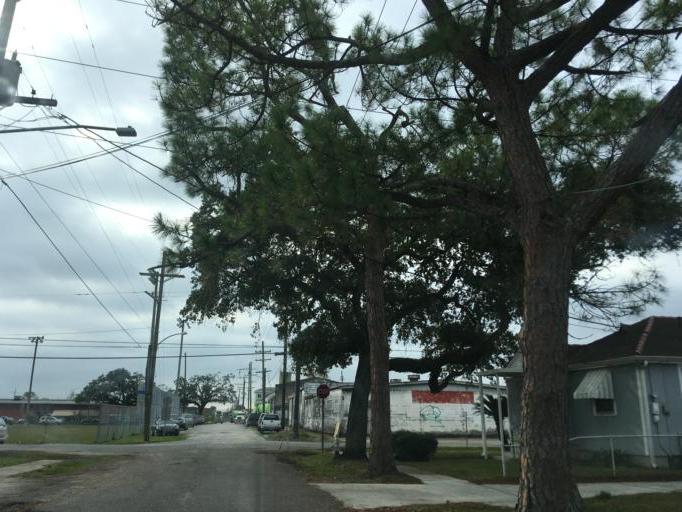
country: US
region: Louisiana
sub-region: Orleans Parish
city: New Orleans
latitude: 29.9889
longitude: -90.0621
